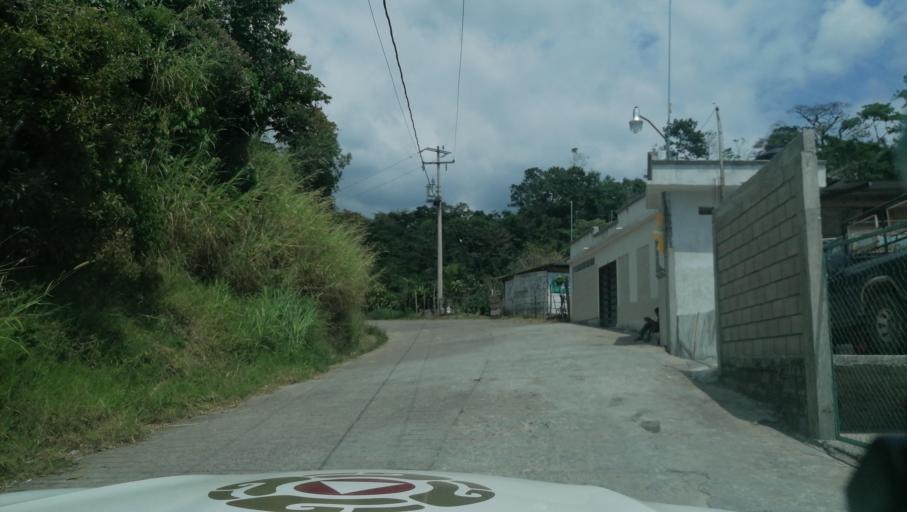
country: MX
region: Chiapas
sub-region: Cacahoatan
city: Benito Juarez
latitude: 15.1113
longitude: -92.2094
